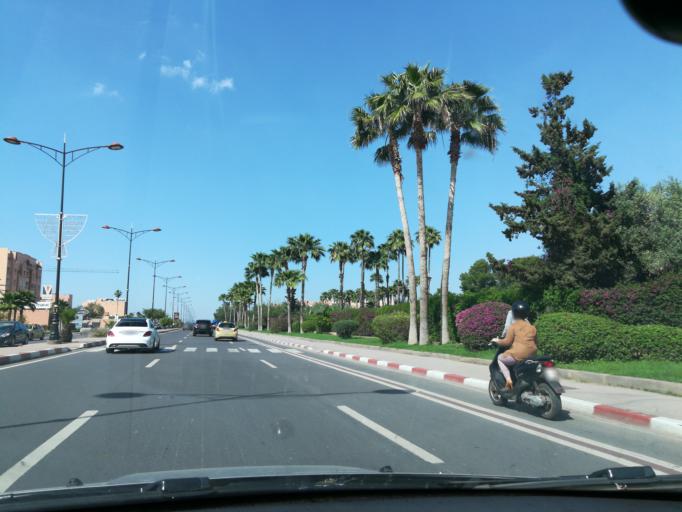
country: MA
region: Marrakech-Tensift-Al Haouz
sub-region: Marrakech
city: Marrakesh
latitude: 31.6613
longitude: -8.0151
